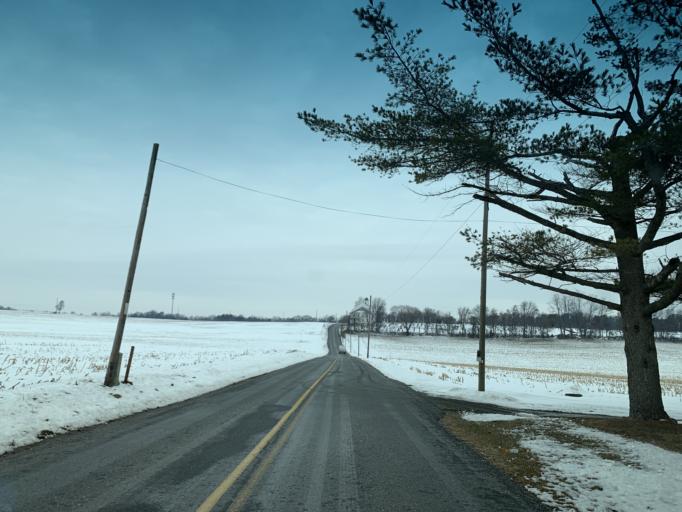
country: US
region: Pennsylvania
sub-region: York County
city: Susquehanna Trails
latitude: 39.7266
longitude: -76.3016
